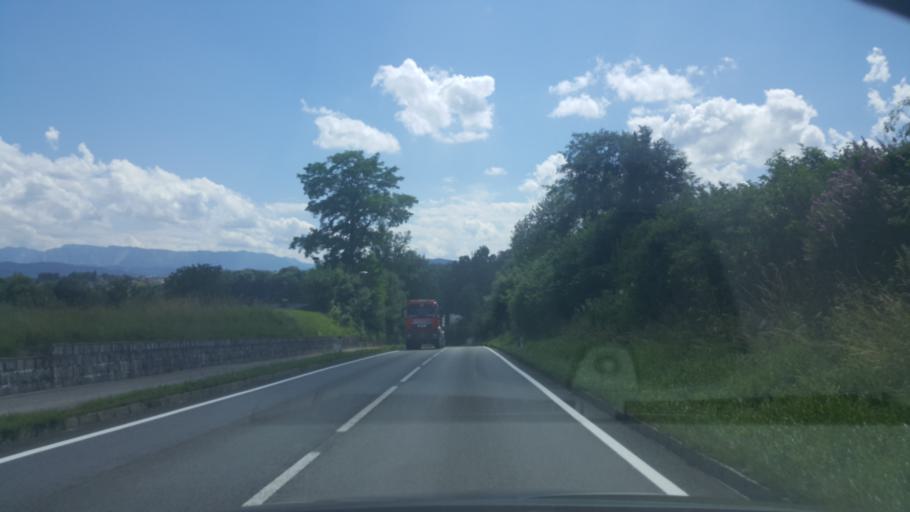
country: AT
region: Upper Austria
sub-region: Politischer Bezirk Vocklabruck
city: Gampern
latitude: 48.0001
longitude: 13.5453
